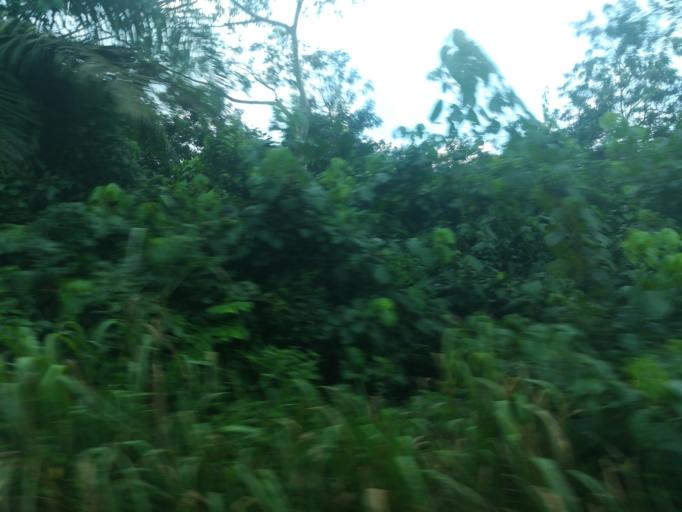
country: NG
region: Lagos
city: Ikorodu
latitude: 6.6655
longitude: 3.6383
